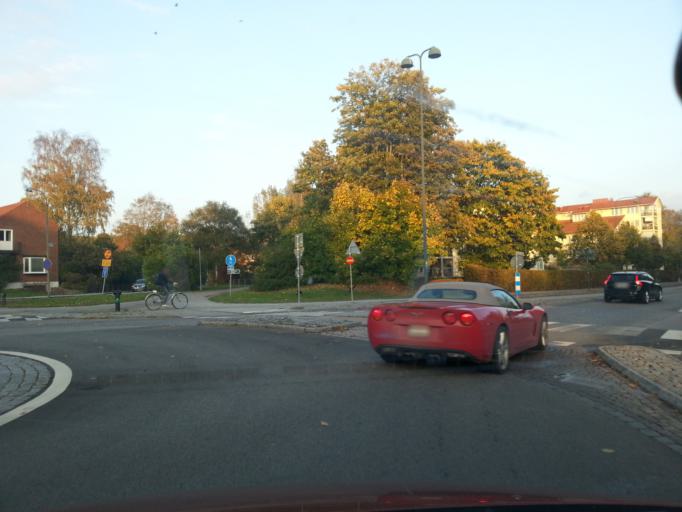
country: SE
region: Skane
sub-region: Lunds Kommun
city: Lund
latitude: 55.7001
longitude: 13.2067
